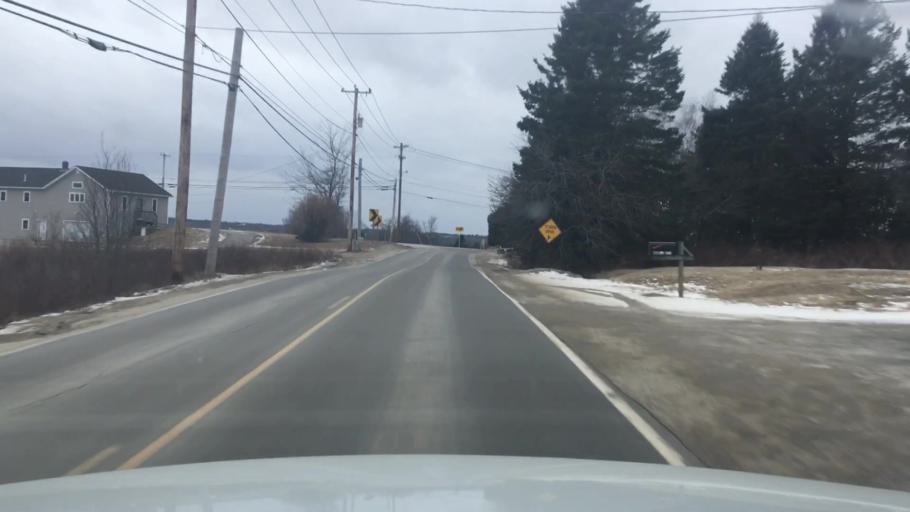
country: US
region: Maine
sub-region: Washington County
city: Addison
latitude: 44.6213
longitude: -67.7102
